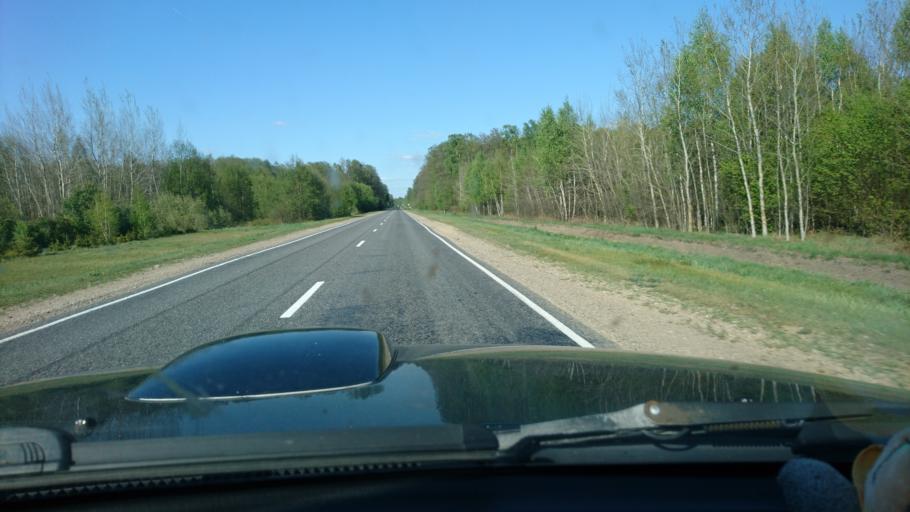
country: BY
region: Brest
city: Zhabinka
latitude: 52.3921
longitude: 24.1723
